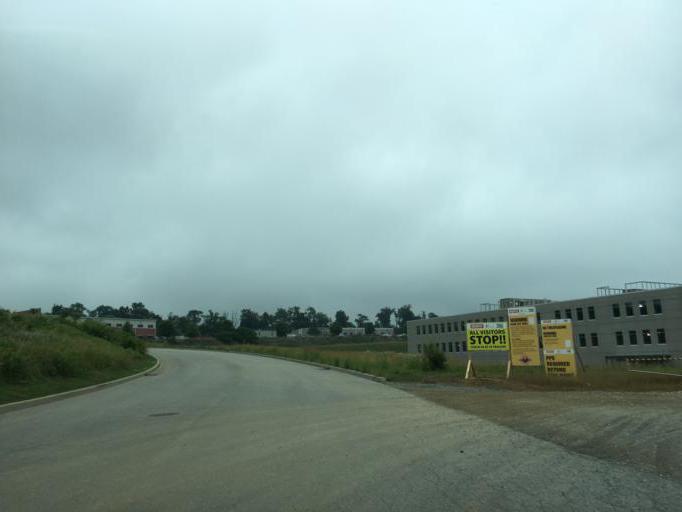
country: US
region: Pennsylvania
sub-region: York County
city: Shrewsbury
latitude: 39.7727
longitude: -76.6601
